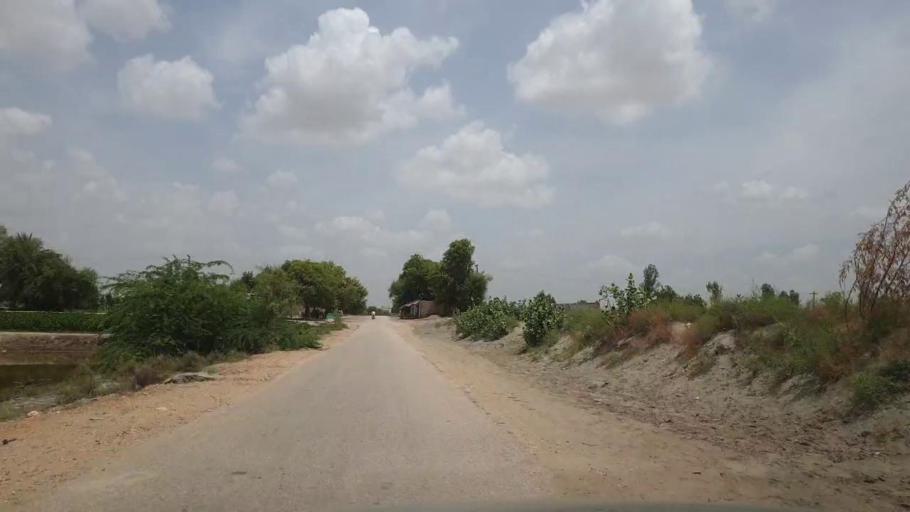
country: PK
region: Sindh
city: Kot Diji
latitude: 27.2012
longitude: 69.0579
